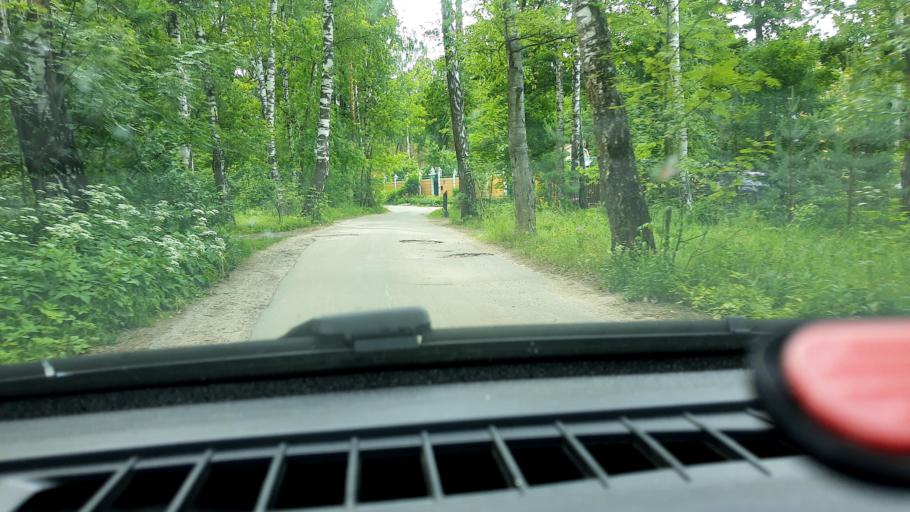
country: RU
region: Nizjnij Novgorod
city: Afonino
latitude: 56.1866
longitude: 44.1037
